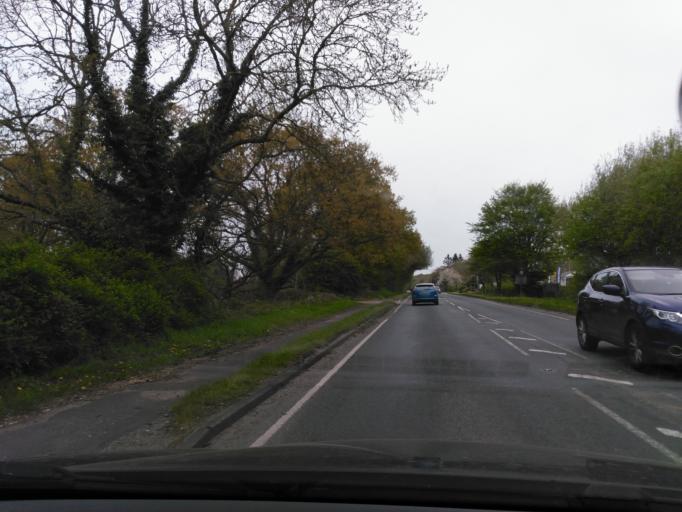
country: GB
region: England
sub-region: Hampshire
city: Tadley
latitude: 51.3295
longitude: -1.1287
